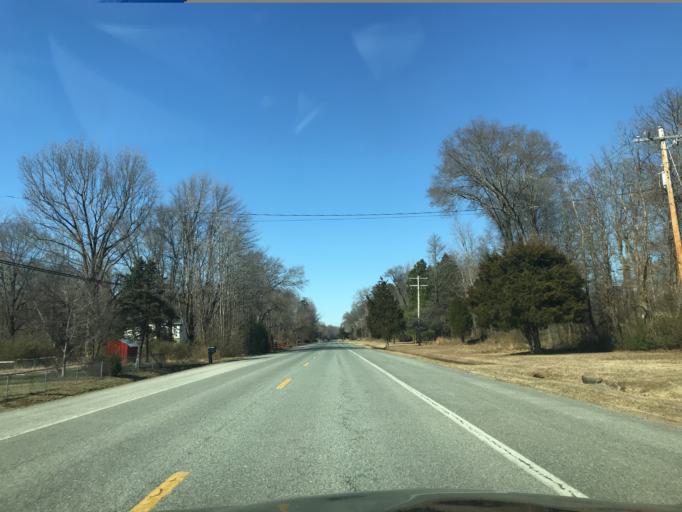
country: US
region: Maryland
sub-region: Charles County
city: Bryans Road
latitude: 38.6656
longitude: -77.0822
